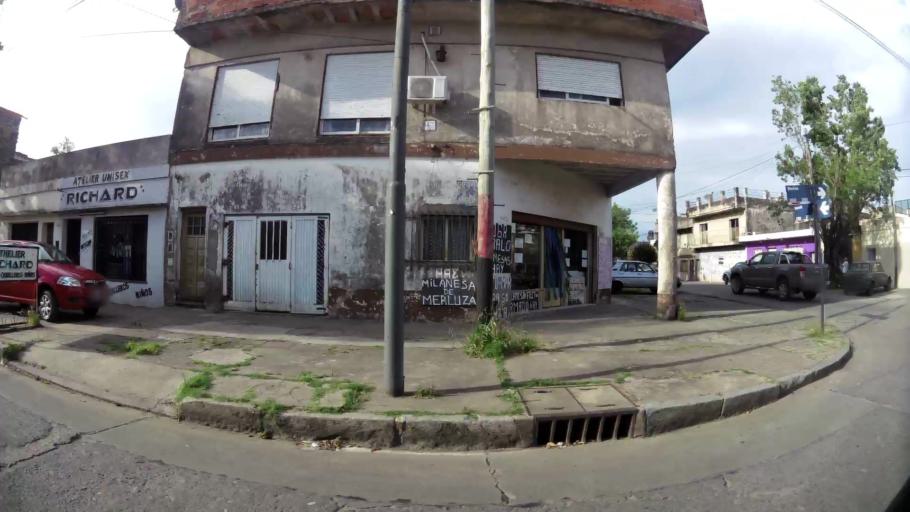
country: AR
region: Santa Fe
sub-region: Departamento de Rosario
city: Rosario
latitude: -32.9757
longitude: -60.6785
